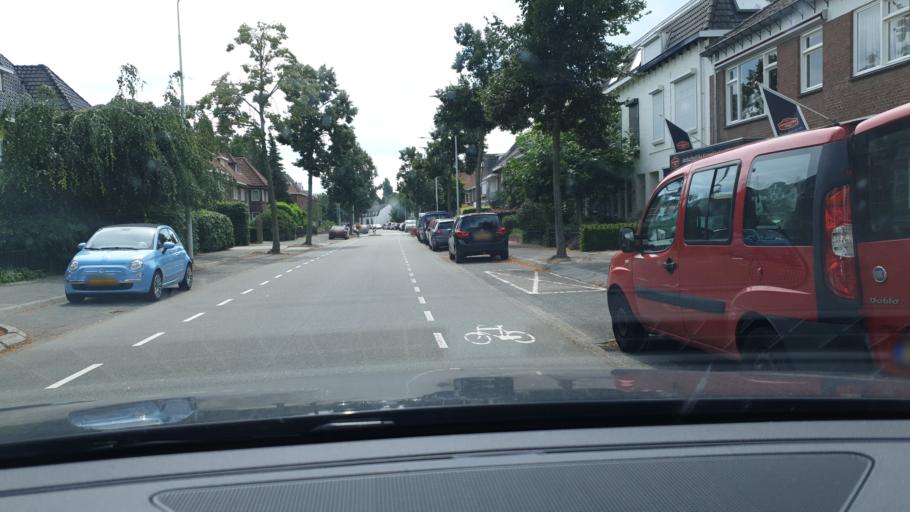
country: NL
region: North Brabant
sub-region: Gemeente Eindhoven
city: Eindhoven
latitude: 51.4294
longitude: 5.4710
